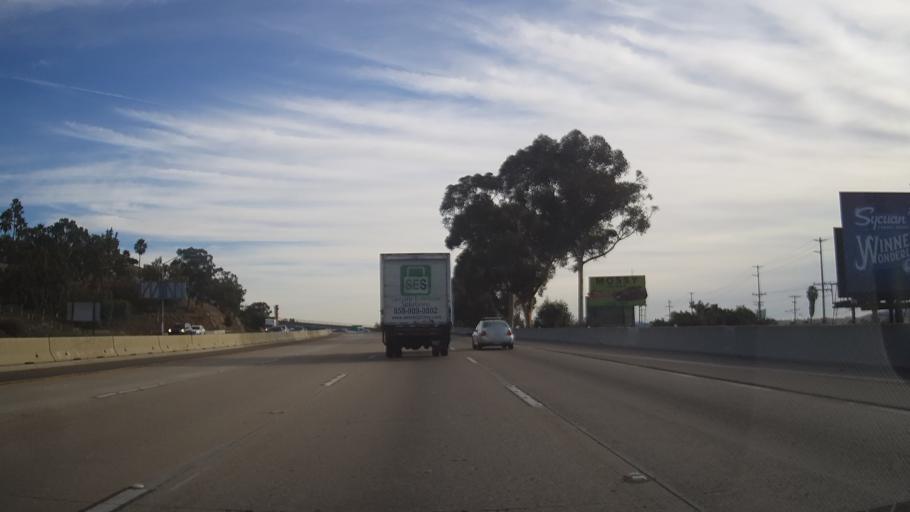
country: US
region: California
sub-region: San Diego County
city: Lemon Grove
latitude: 32.7458
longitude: -117.0367
